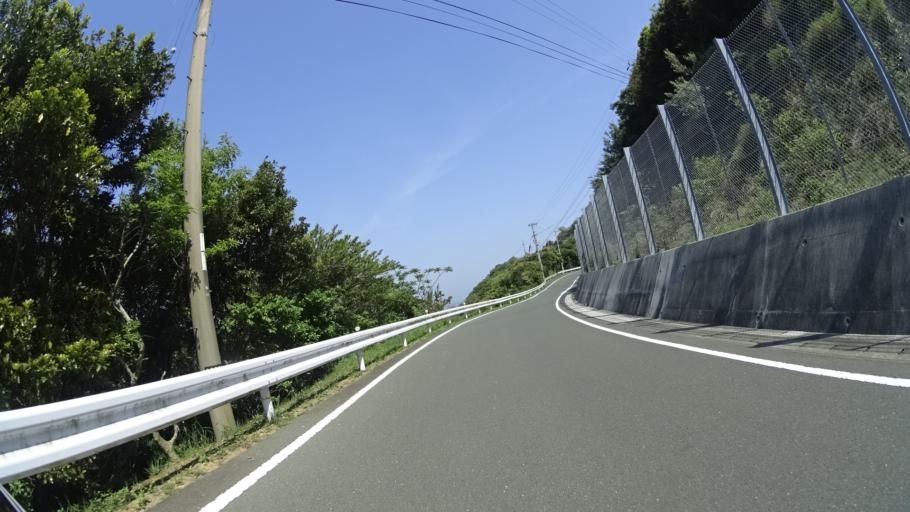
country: JP
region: Oita
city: Tsukumiura
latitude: 33.3568
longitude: 132.0379
